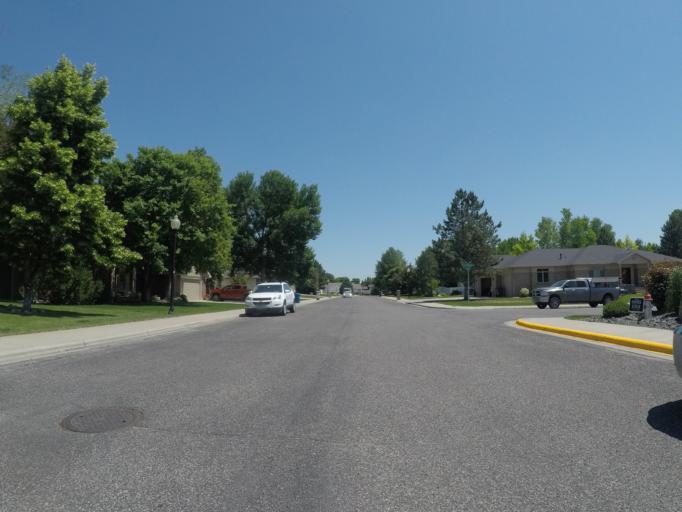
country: US
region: Montana
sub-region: Yellowstone County
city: Billings
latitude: 45.7909
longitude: -108.5799
